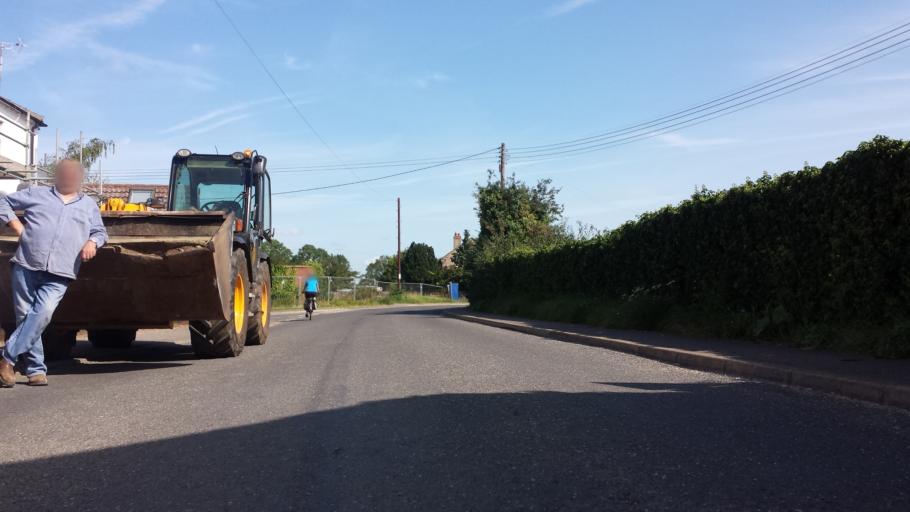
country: GB
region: England
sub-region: Cambridgeshire
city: Isleham
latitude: 52.3560
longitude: 0.4538
